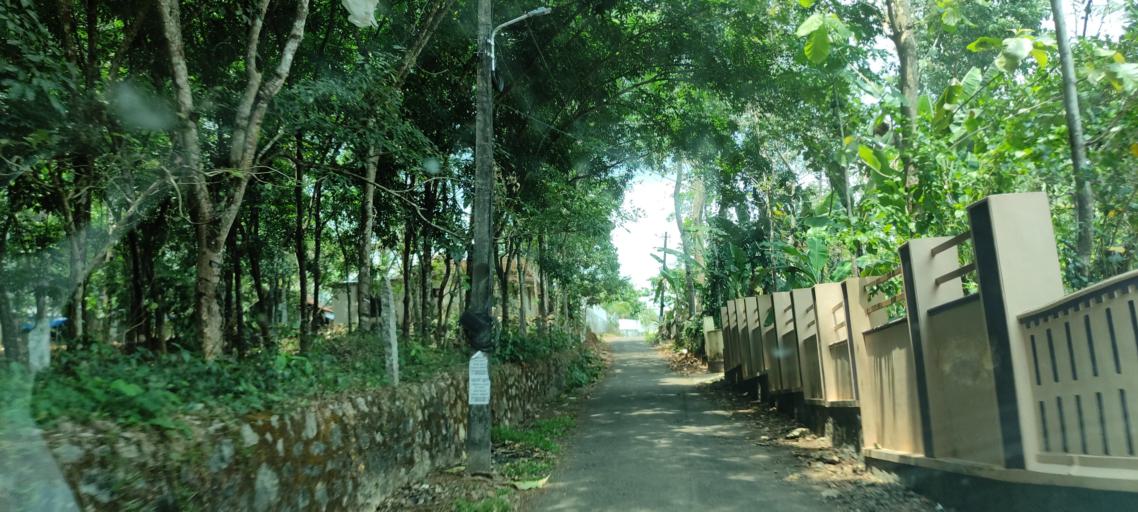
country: IN
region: Kerala
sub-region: Pattanamtitta
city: Adur
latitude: 9.1717
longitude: 76.7467
